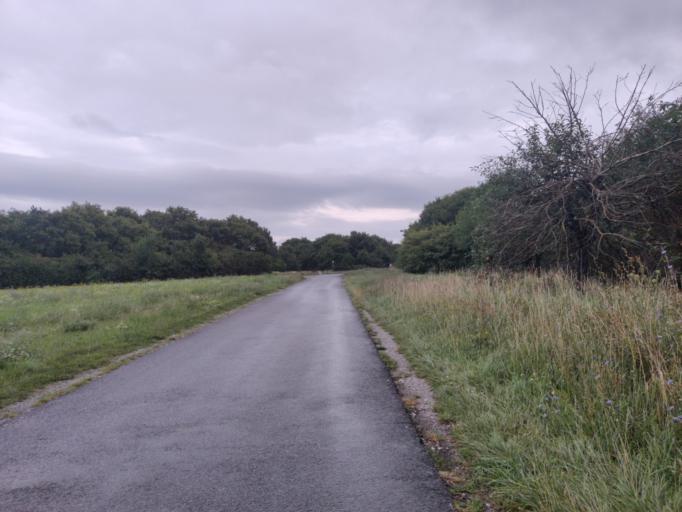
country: AT
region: Lower Austria
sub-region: Politischer Bezirk Korneuburg
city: Langenzersdorf
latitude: 48.2786
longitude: 16.3610
